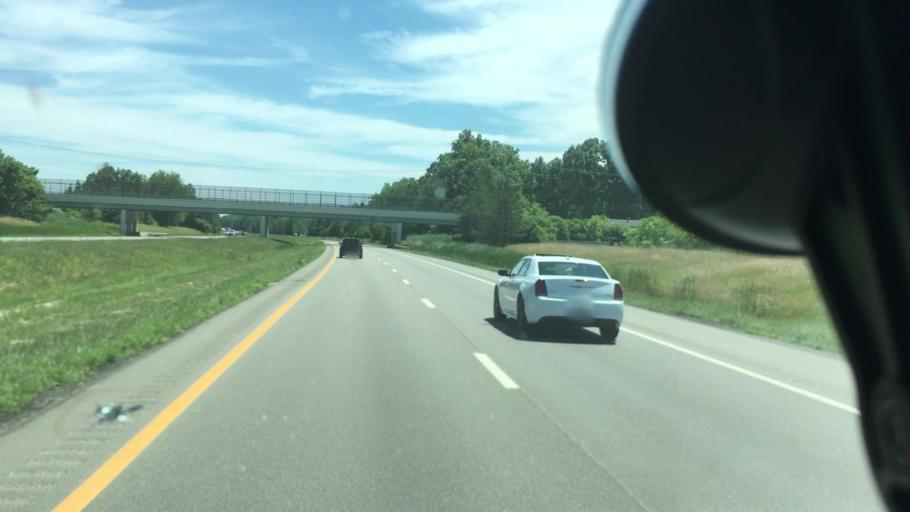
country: US
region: Ohio
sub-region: Mahoning County
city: Austintown
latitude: 41.0704
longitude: -80.7527
